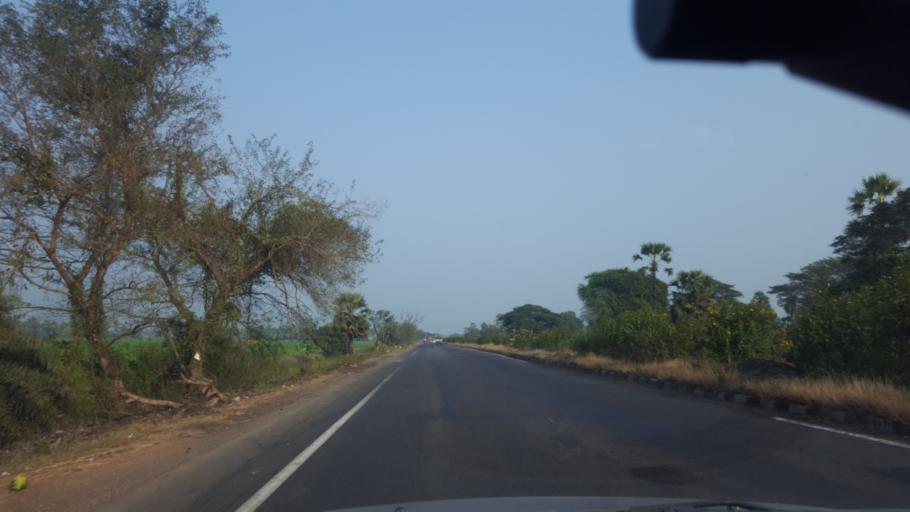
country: IN
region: Andhra Pradesh
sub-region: West Godavari
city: Tadepallegudem
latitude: 16.8102
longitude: 81.3419
